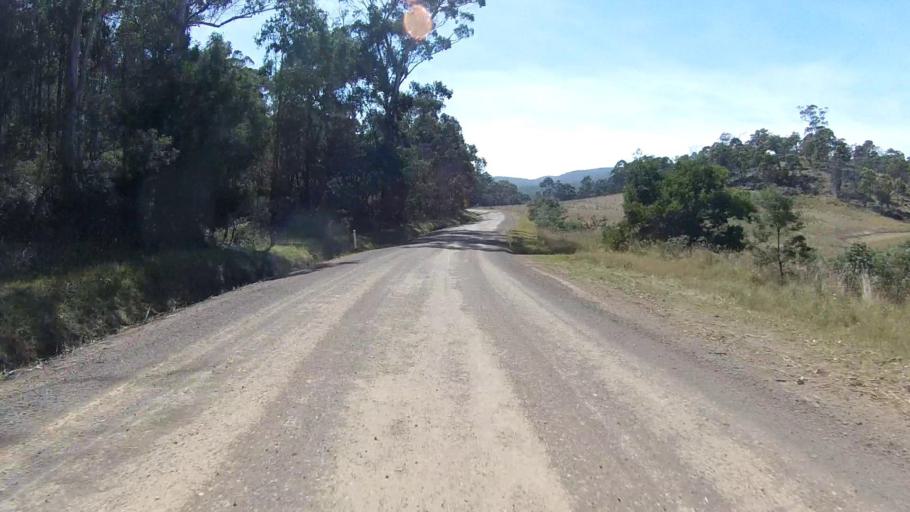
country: AU
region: Tasmania
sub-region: Sorell
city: Sorell
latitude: -42.7535
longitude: 147.6882
